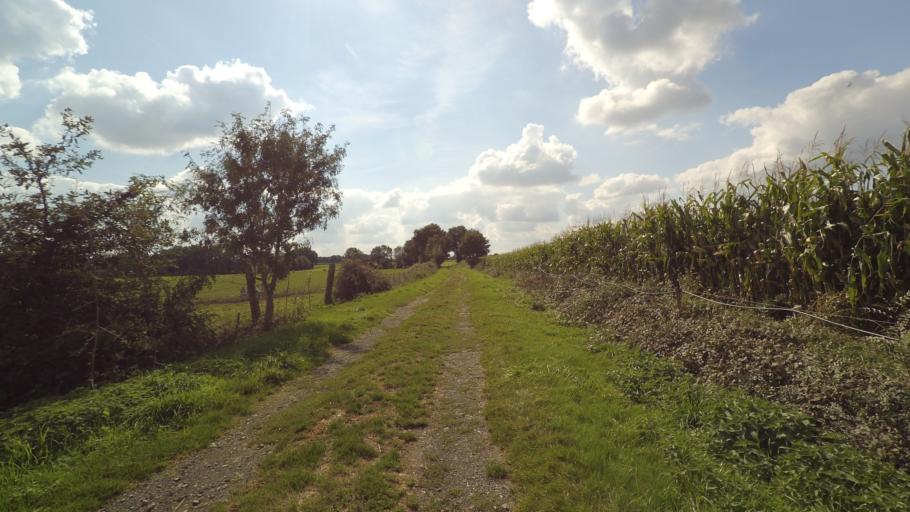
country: FR
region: Pays de la Loire
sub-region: Departement de la Vendee
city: Bouffere
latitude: 46.9523
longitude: -1.3762
